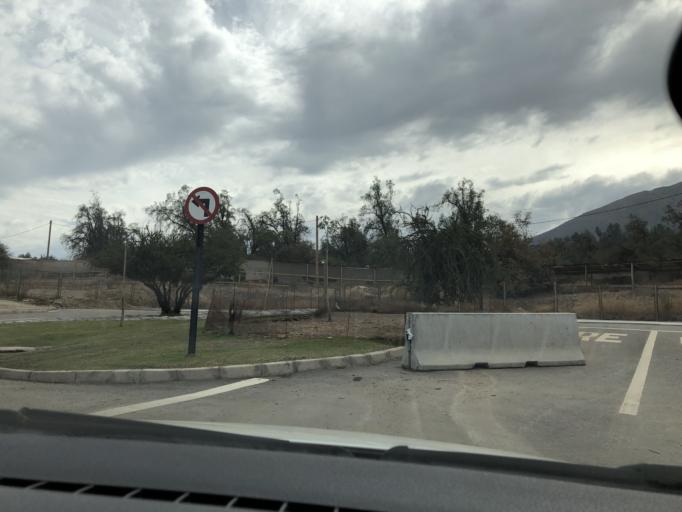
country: CL
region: Santiago Metropolitan
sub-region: Provincia de Cordillera
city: Puente Alto
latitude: -33.5803
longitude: -70.5084
